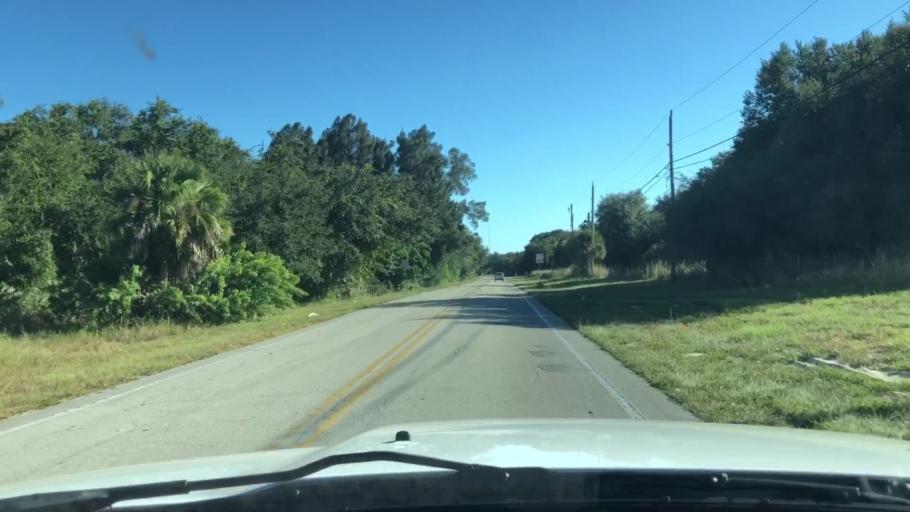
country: US
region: Florida
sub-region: Indian River County
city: Florida Ridge
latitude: 27.5704
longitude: -80.3743
